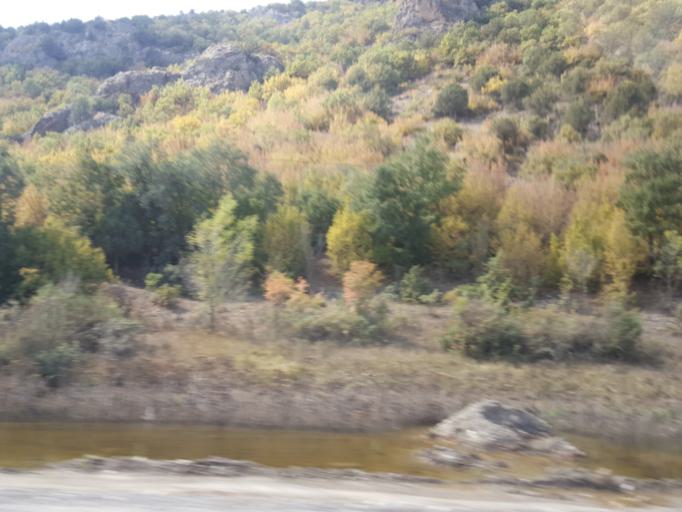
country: TR
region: Yozgat
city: Cekerek
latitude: 40.1126
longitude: 35.6161
